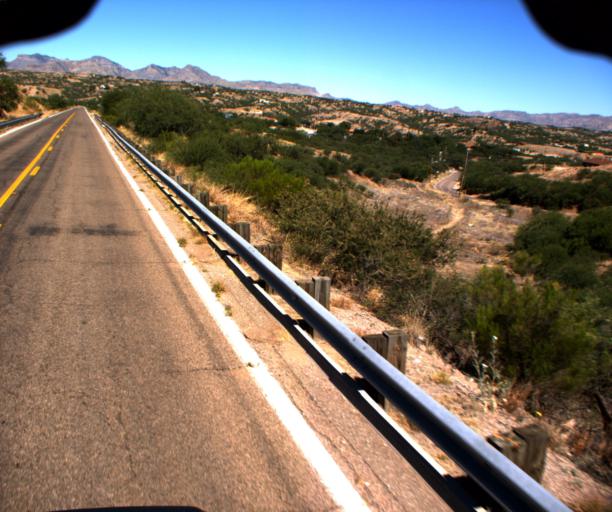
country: US
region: Arizona
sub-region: Santa Cruz County
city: Rio Rico
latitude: 31.4297
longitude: -110.9923
